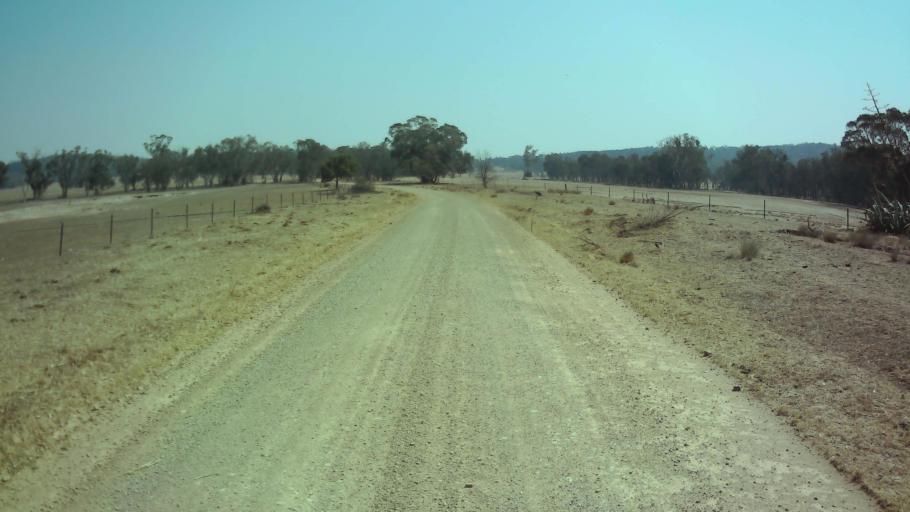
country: AU
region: New South Wales
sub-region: Weddin
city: Grenfell
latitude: -33.6749
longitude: 148.2756
